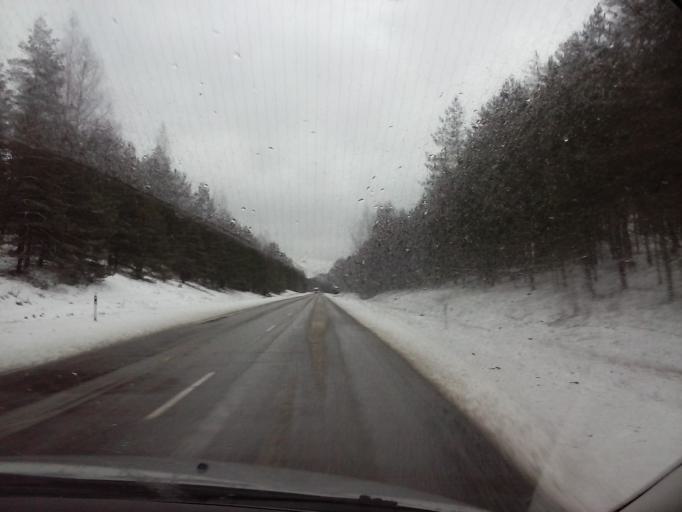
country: LV
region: Strenci
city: Seda
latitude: 57.6324
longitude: 25.8155
